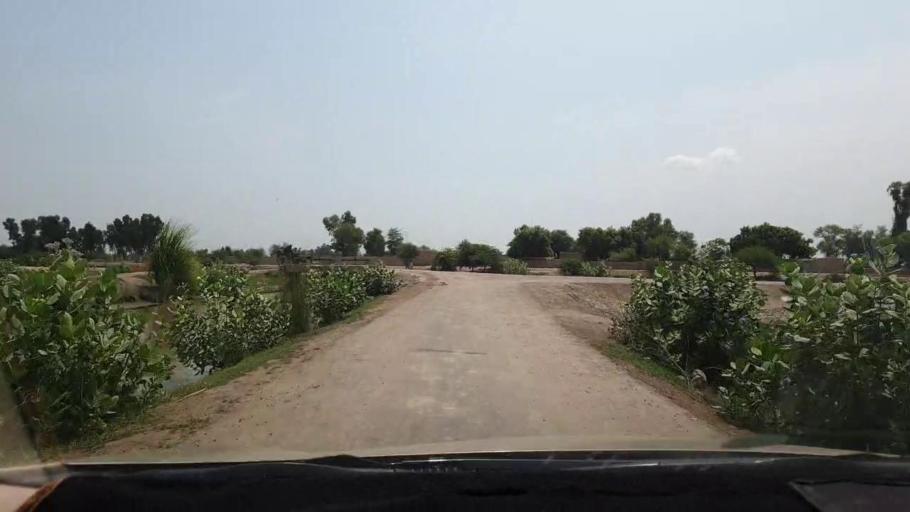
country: PK
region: Sindh
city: Naudero
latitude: 27.6578
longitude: 68.3317
